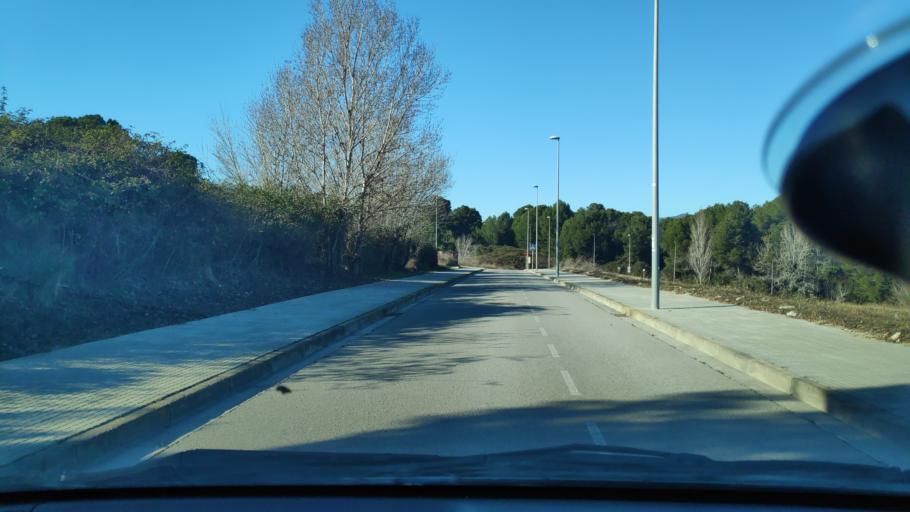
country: ES
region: Catalonia
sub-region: Provincia de Barcelona
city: Sant Quirze del Valles
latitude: 41.5368
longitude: 2.0586
